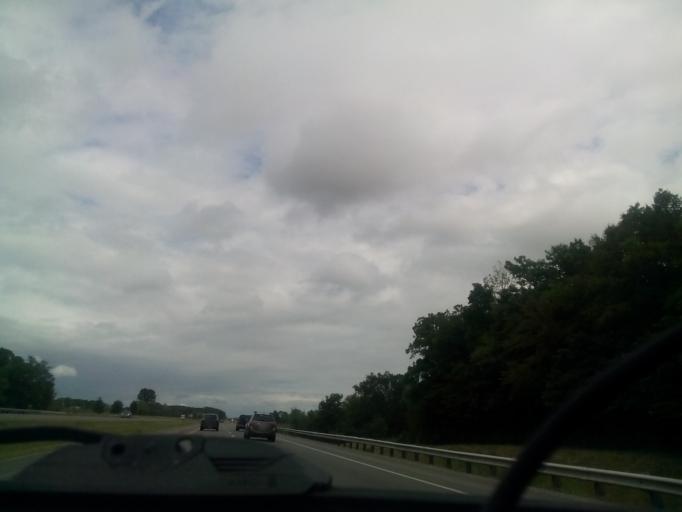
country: US
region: Ohio
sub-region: Williams County
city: Montpelier
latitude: 41.6277
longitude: -84.7242
